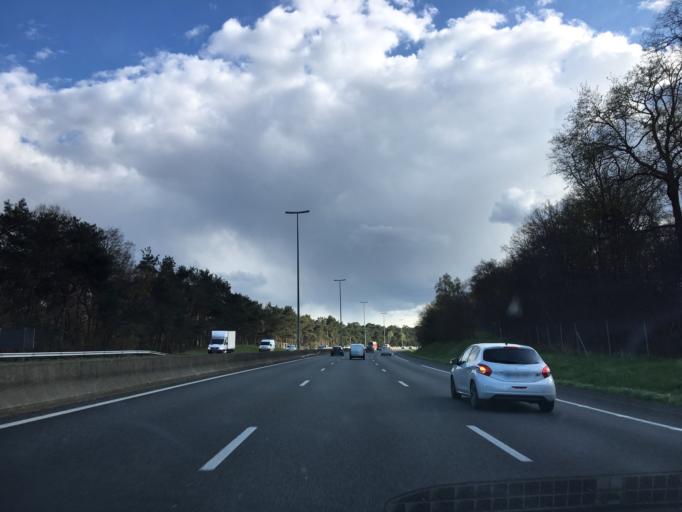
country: FR
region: Picardie
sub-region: Departement de l'Oise
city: Senlis
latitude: 49.1833
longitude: 2.6053
